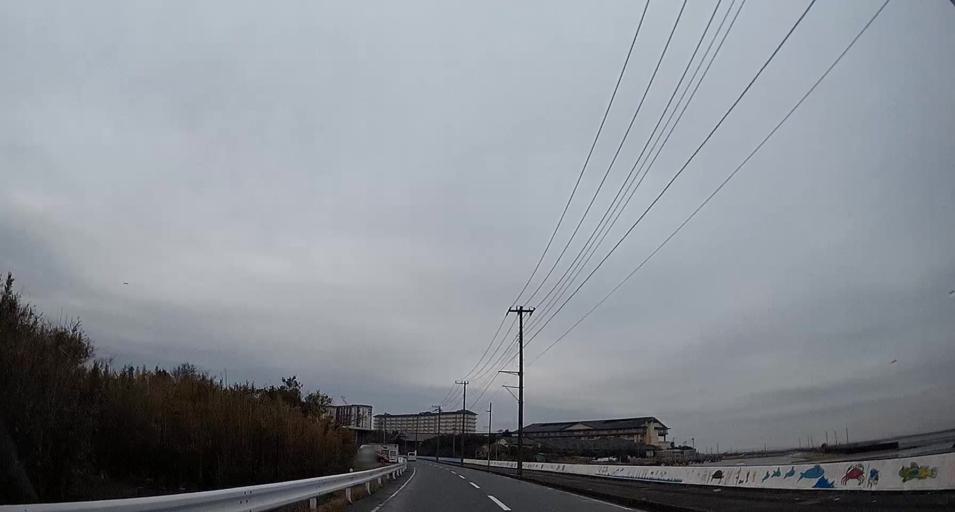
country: JP
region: Chiba
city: Kisarazu
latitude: 35.4245
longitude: 139.9013
